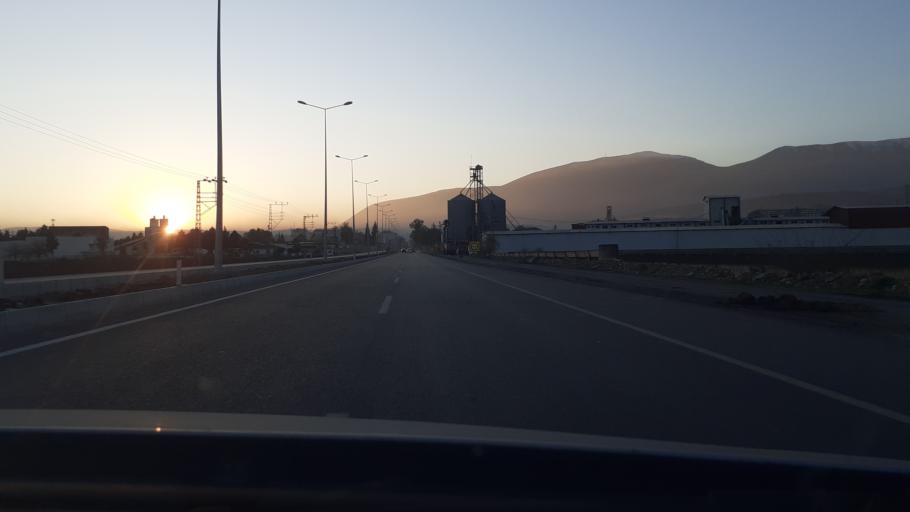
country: TR
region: Hatay
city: Kirikhan
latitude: 36.5012
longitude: 36.3827
